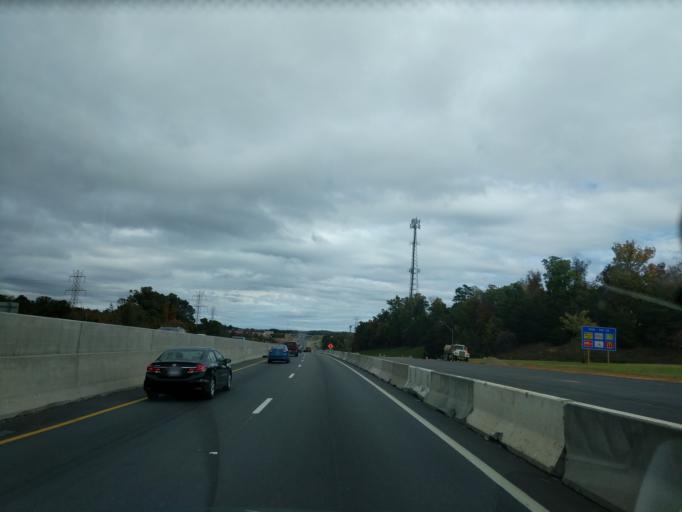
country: US
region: North Carolina
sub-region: Cabarrus County
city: Kannapolis
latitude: 35.4513
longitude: -80.5966
